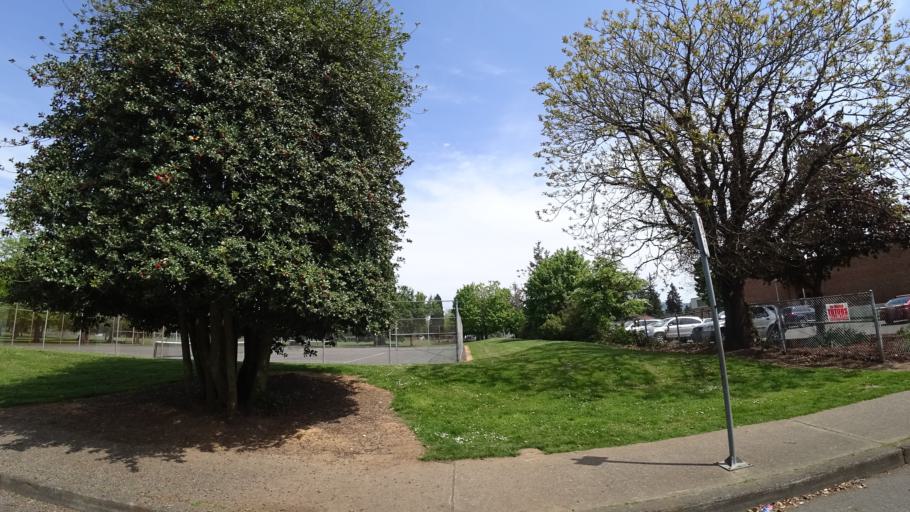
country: US
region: Oregon
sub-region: Multnomah County
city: Lents
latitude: 45.4722
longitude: -122.6022
